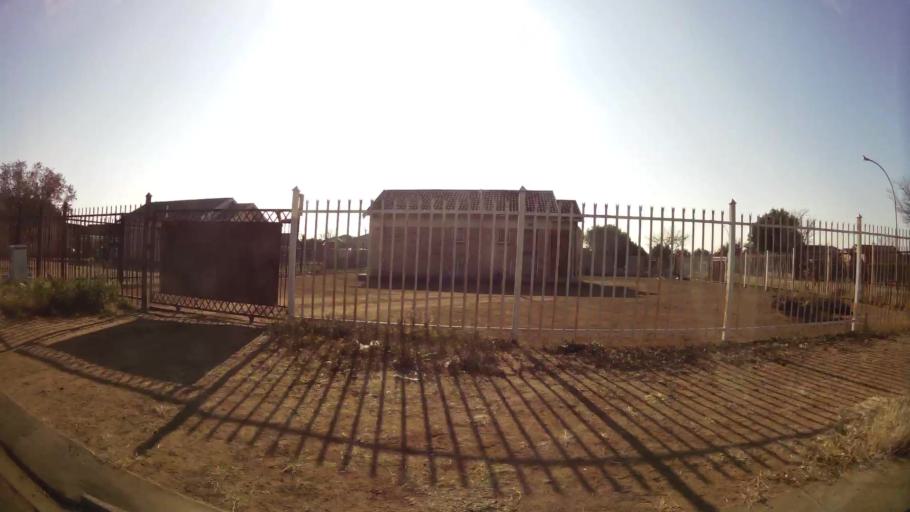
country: ZA
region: Orange Free State
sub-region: Mangaung Metropolitan Municipality
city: Bloemfontein
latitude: -29.1849
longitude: 26.1732
